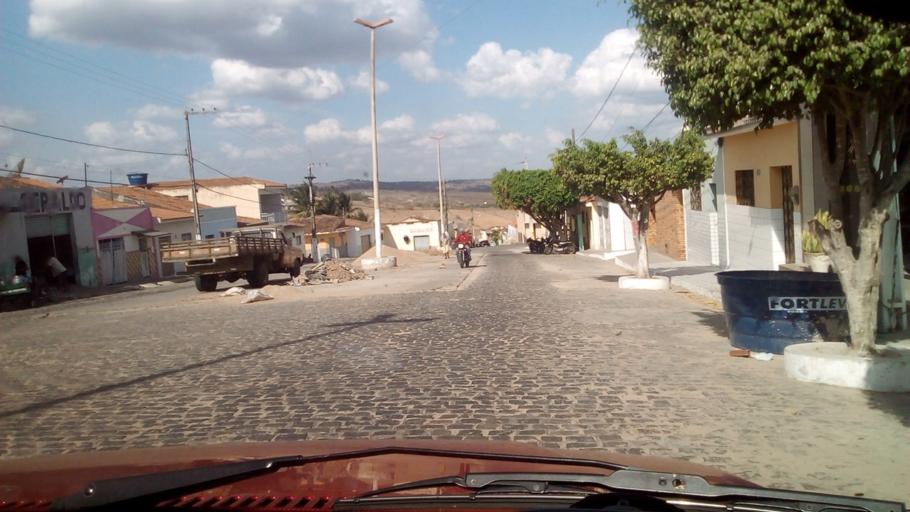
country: BR
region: Paraiba
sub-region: Arara
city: Arara
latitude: -6.8288
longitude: -35.7590
